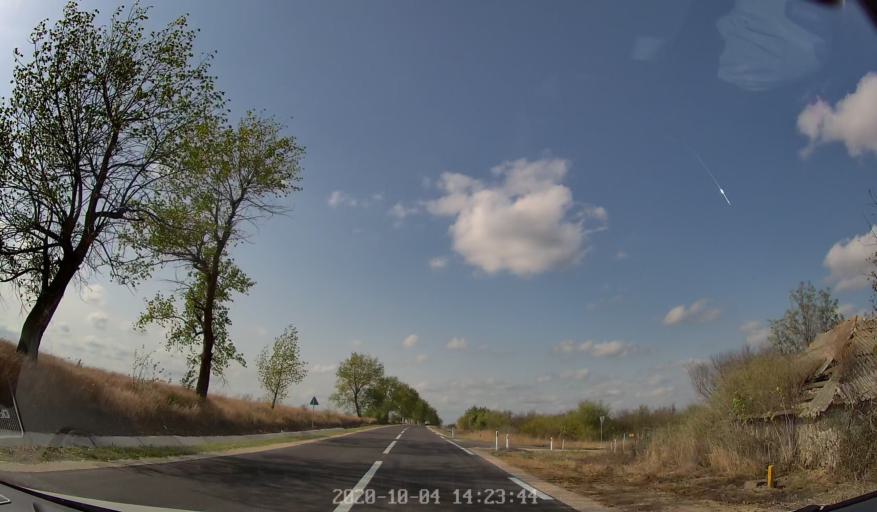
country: MD
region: Rezina
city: Saharna
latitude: 47.6106
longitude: 28.9305
